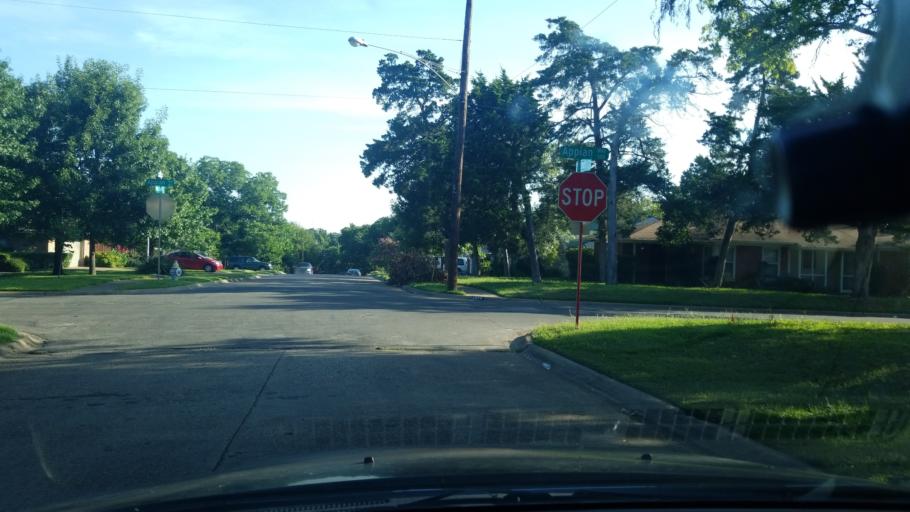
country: US
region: Texas
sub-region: Dallas County
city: Dallas
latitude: 32.7311
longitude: -96.8168
